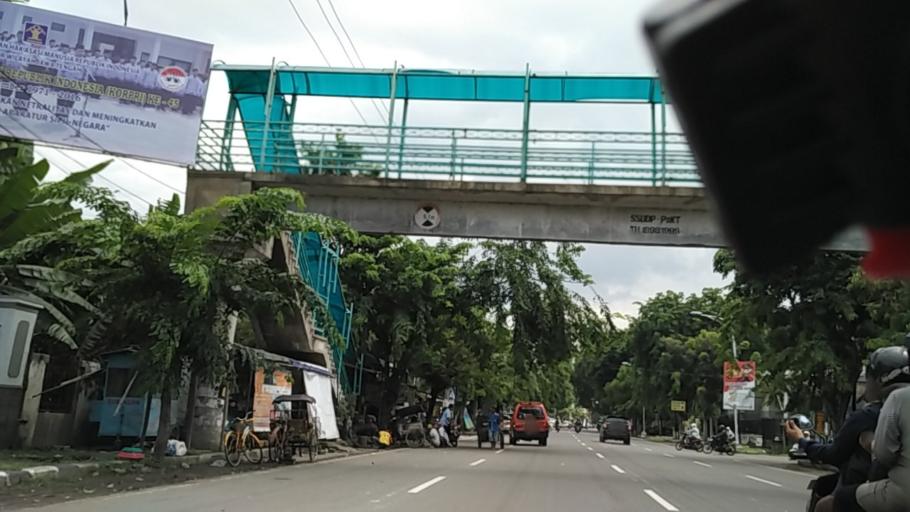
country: ID
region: Central Java
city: Semarang
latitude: -6.9751
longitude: 110.4348
